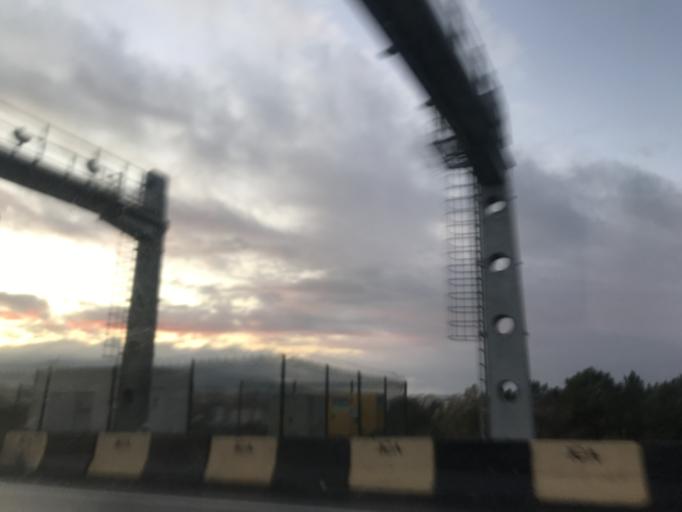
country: TR
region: Istanbul
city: Sultanbeyli
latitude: 40.9517
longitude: 29.3138
